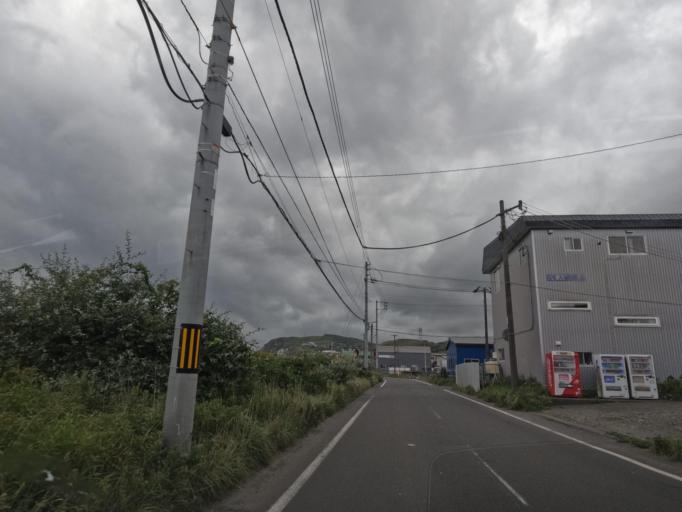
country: JP
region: Hokkaido
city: Muroran
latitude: 42.3383
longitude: 141.0288
